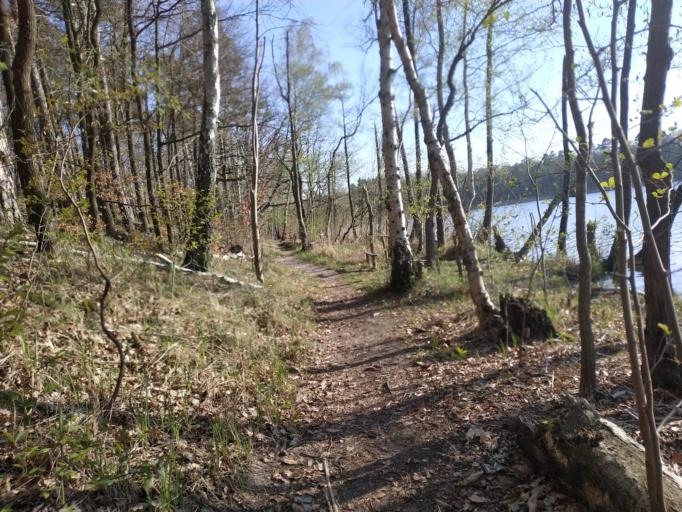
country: DE
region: Brandenburg
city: Strausberg
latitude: 52.5682
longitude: 13.8312
